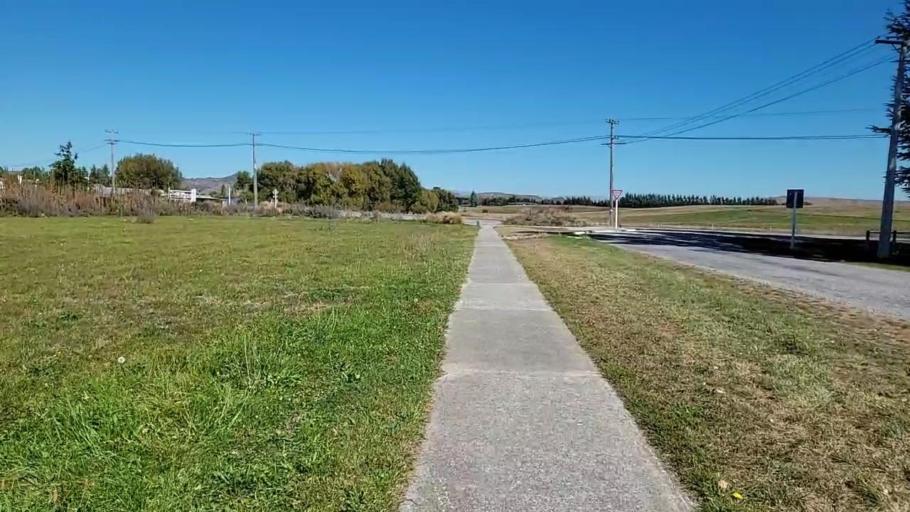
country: NZ
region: Otago
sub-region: Queenstown-Lakes District
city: Wanaka
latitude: -45.0917
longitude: 169.6027
